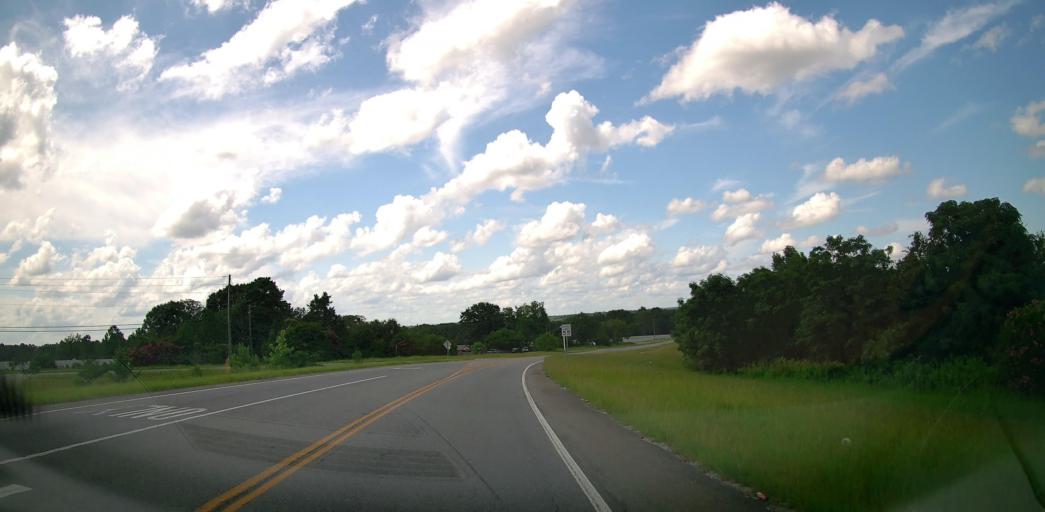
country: US
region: Georgia
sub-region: Houston County
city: Centerville
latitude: 32.6804
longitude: -83.7002
